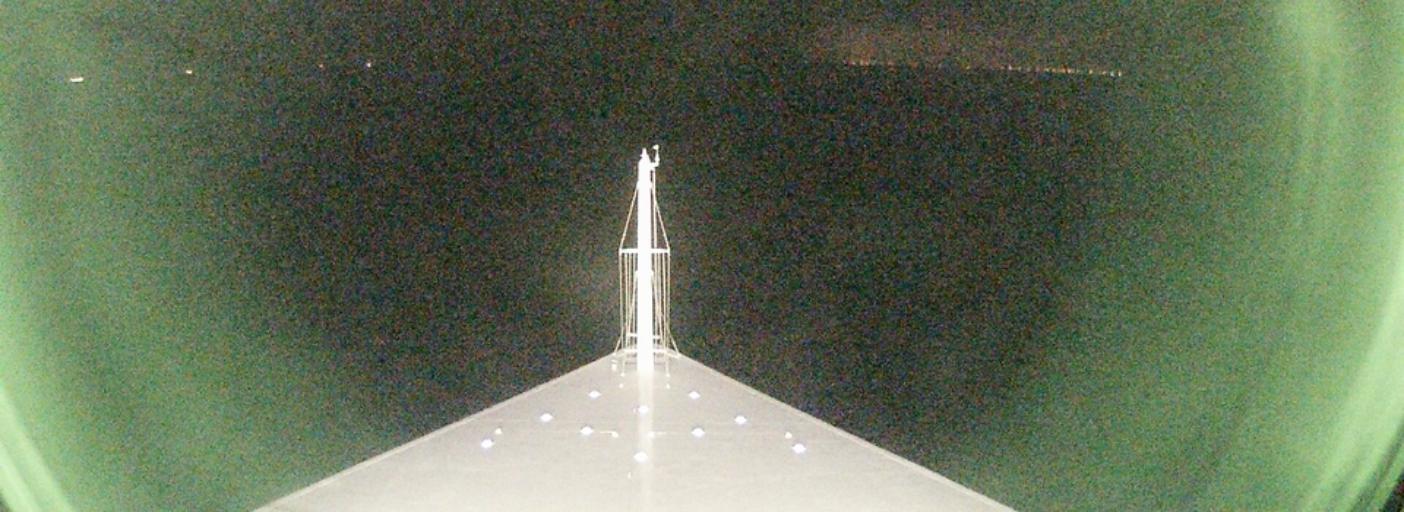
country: DE
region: Lower Saxony
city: Langeoog
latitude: 53.9753
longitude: 7.3938
